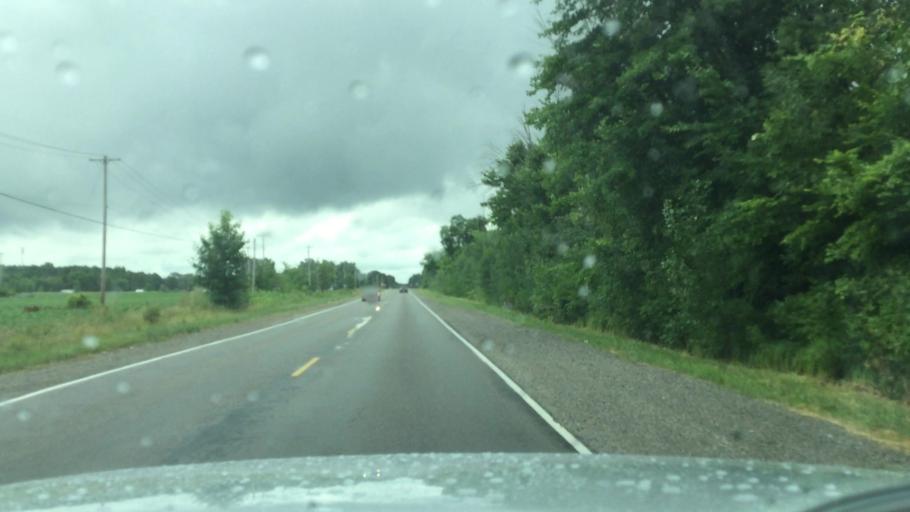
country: US
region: Michigan
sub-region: Genesee County
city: Flushing
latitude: 43.0734
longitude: -83.7732
